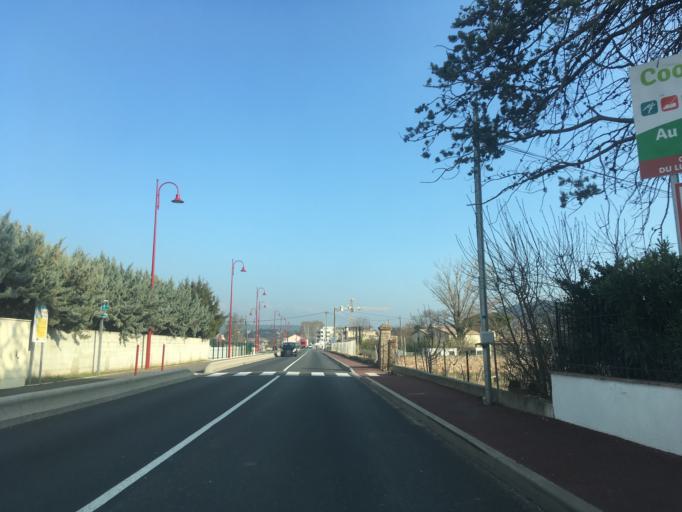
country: FR
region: Provence-Alpes-Cote d'Azur
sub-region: Departement du Var
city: Vidauban
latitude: 43.4201
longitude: 6.4244
